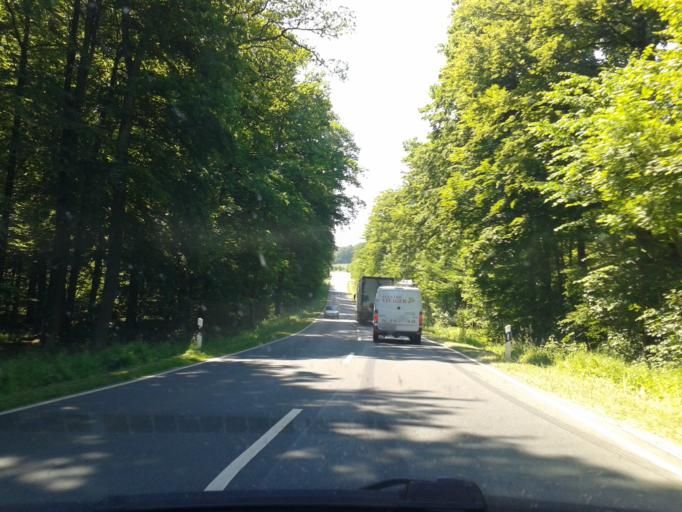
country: DE
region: North Rhine-Westphalia
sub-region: Regierungsbezirk Detmold
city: Bad Meinberg
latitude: 51.8980
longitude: 9.0191
